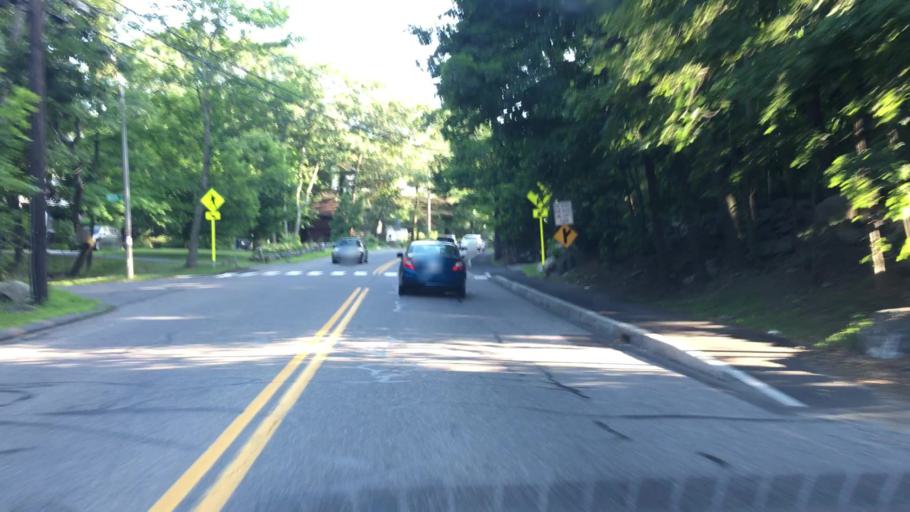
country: US
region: Massachusetts
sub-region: Middlesex County
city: Lexington
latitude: 42.4233
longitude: -71.2085
